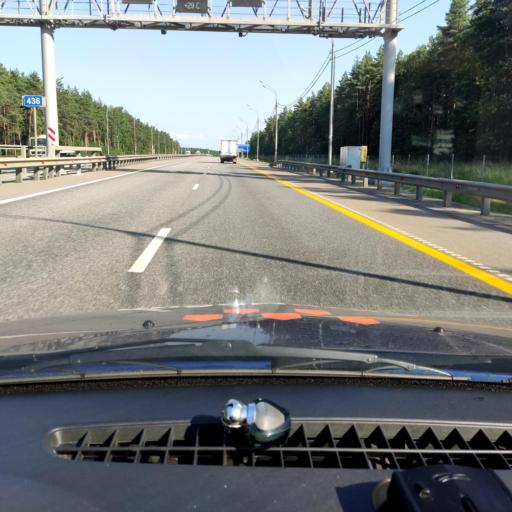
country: RU
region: Lipetsk
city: Zadonsk
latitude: 52.3215
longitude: 39.0321
